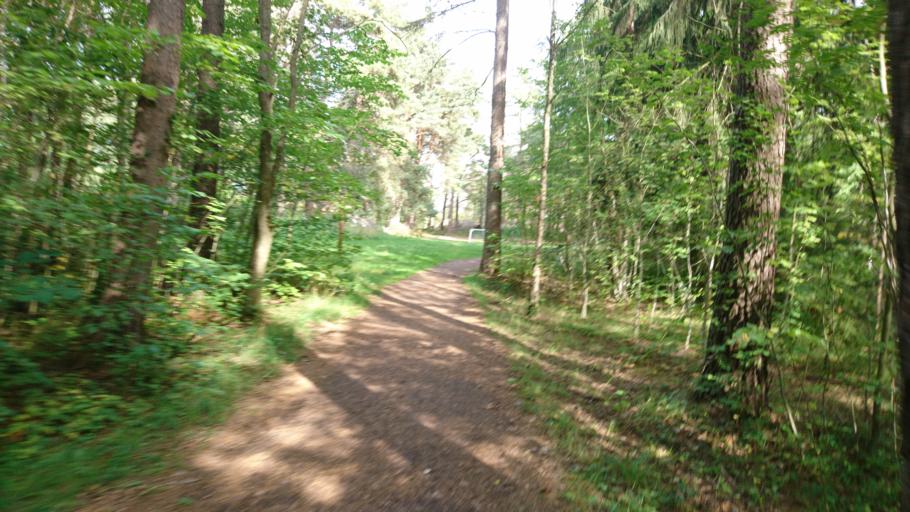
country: SE
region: Uppsala
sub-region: Uppsala Kommun
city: Uppsala
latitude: 59.8458
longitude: 17.6212
